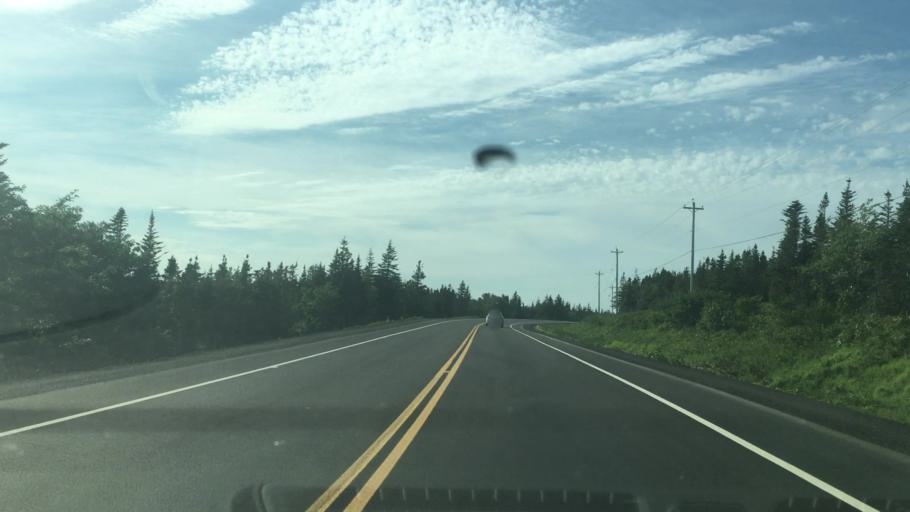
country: CA
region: Nova Scotia
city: Sydney Mines
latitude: 46.8442
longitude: -60.4055
